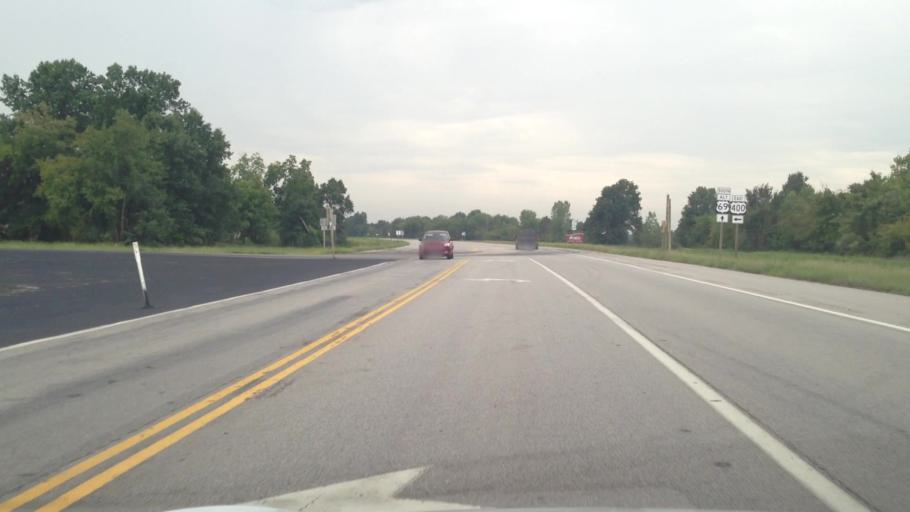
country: US
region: Kansas
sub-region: Cherokee County
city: Baxter Springs
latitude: 37.0559
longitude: -94.7350
